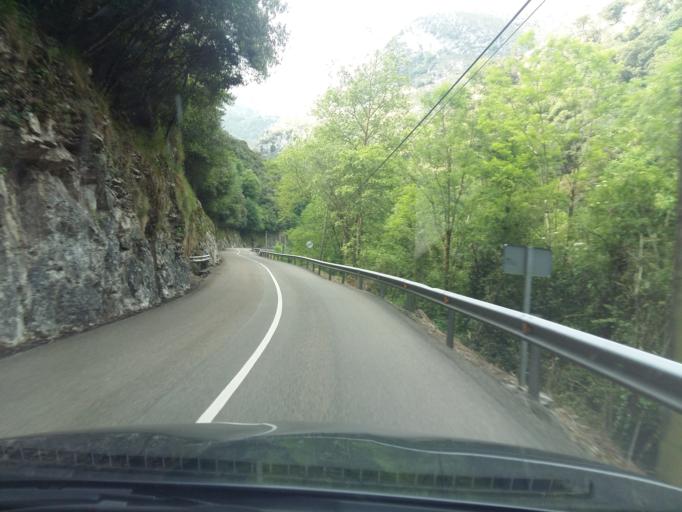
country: ES
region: Cantabria
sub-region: Provincia de Cantabria
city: Tresviso
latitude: 43.3129
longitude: -4.6089
